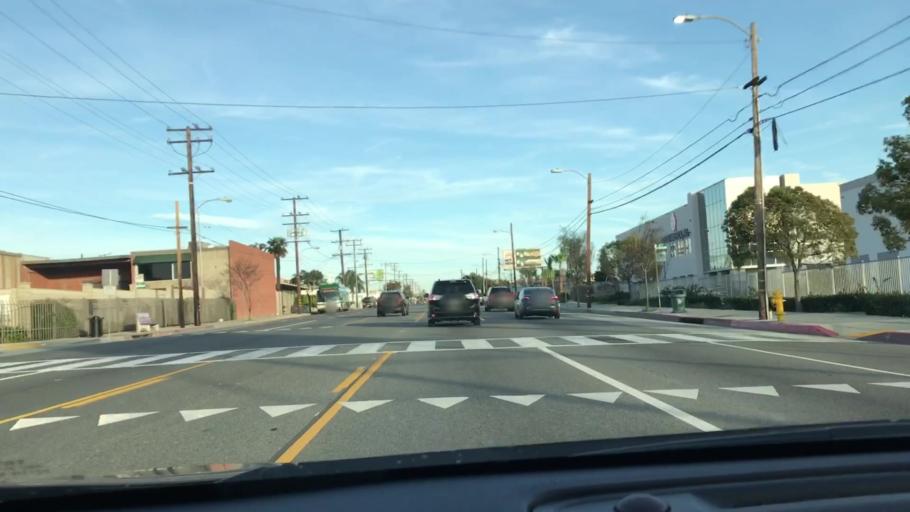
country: US
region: California
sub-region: Los Angeles County
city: West Athens
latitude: 33.9164
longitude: -118.3069
